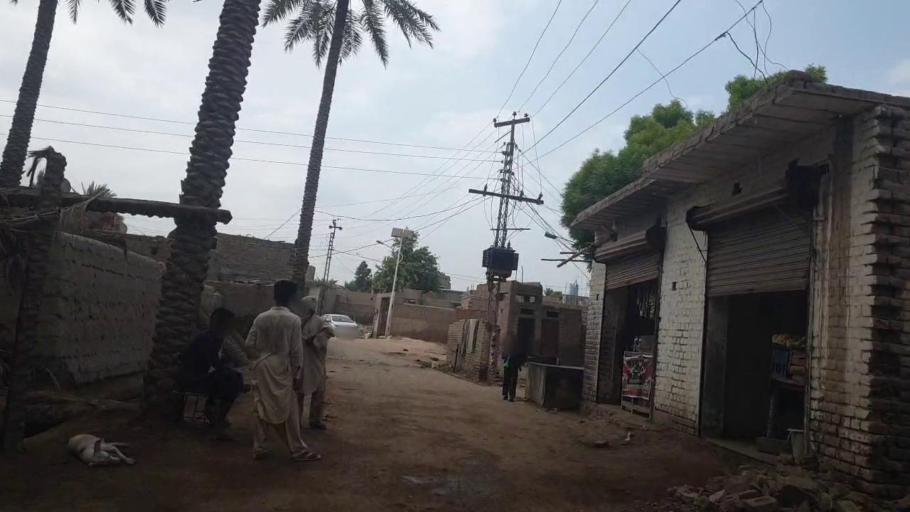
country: PK
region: Sindh
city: Sukkur
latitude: 27.6378
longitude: 68.7906
